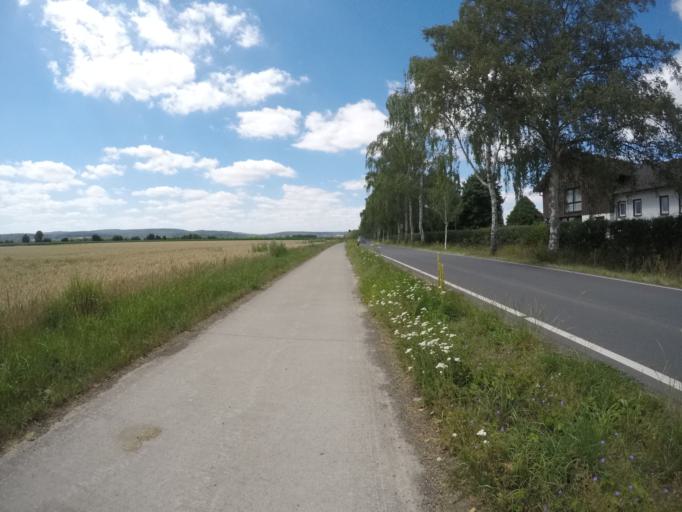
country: DE
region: Lower Saxony
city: Rinteln
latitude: 52.1857
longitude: 9.0578
